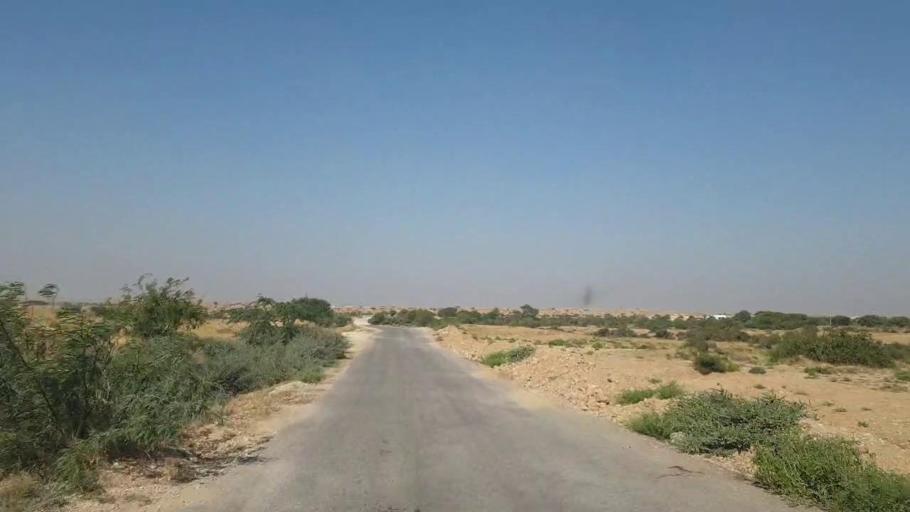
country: PK
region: Sindh
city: Thatta
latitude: 25.2106
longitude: 67.7970
